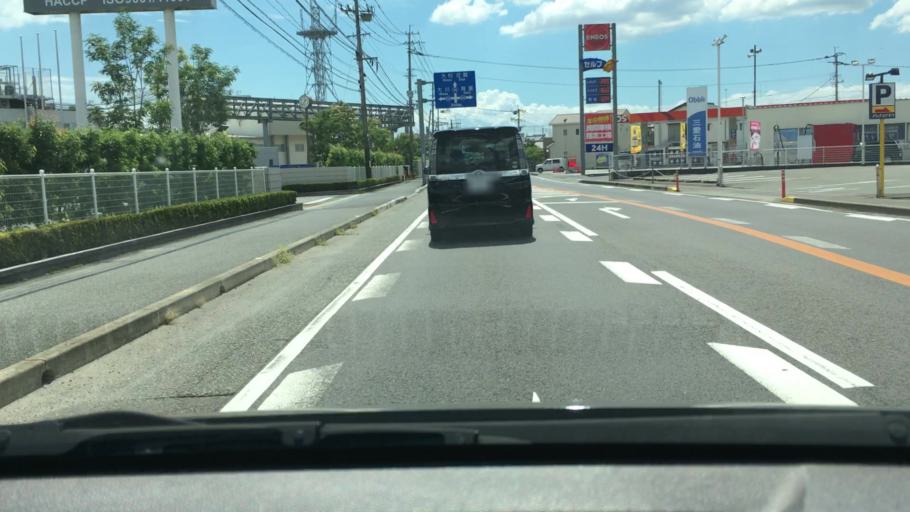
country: JP
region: Saga Prefecture
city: Kanzakimachi-kanzaki
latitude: 33.3151
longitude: 130.3777
